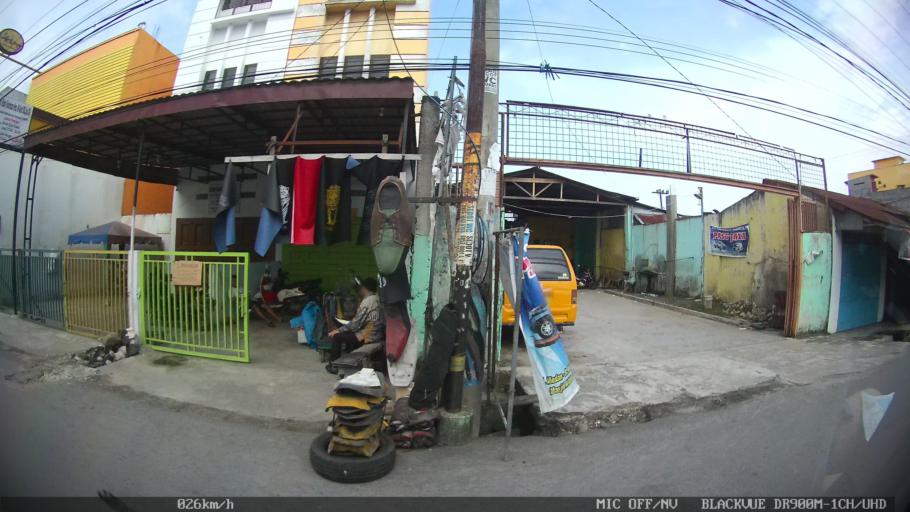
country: ID
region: North Sumatra
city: Medan
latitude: 3.6049
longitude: 98.7577
